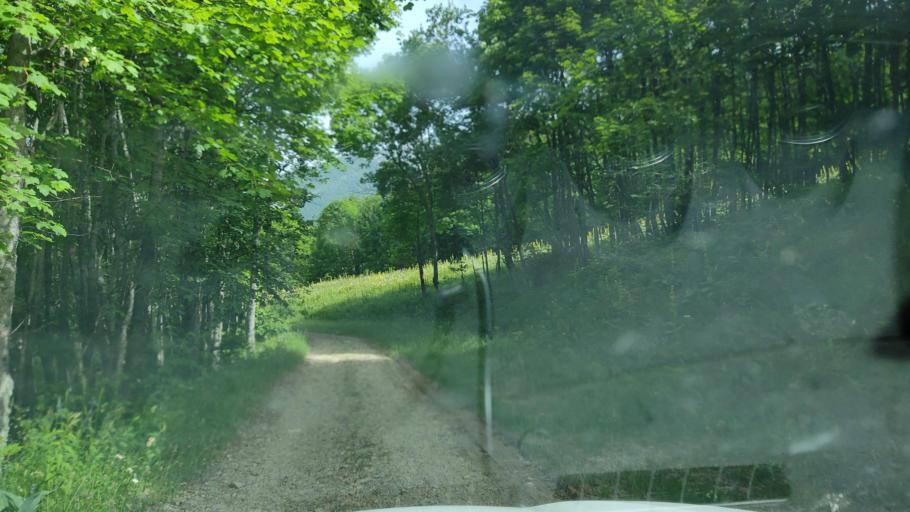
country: FR
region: Rhone-Alpes
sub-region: Departement de la Savoie
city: Cruet
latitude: 45.5921
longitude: 6.1056
